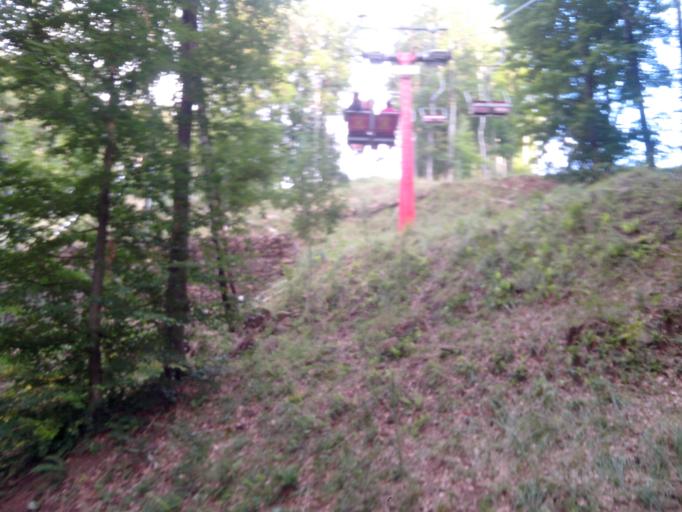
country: RO
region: Maramures
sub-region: Comuna Sisesti
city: Surdesti
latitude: 47.6738
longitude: 23.7814
